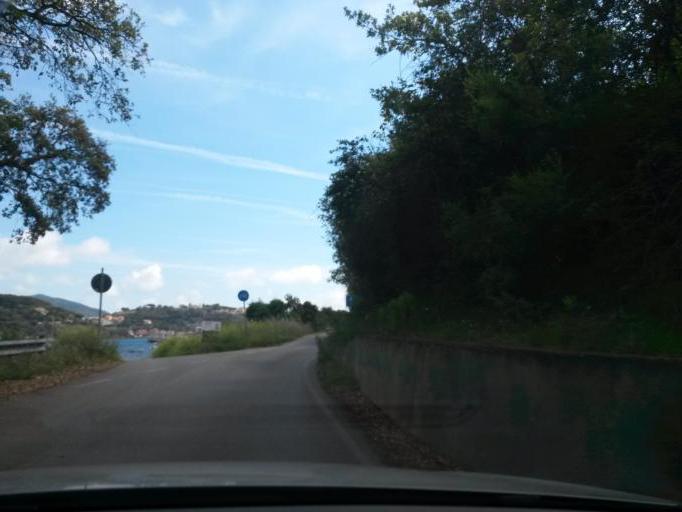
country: IT
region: Tuscany
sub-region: Provincia di Livorno
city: Porto Azzurro
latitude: 42.7576
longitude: 10.3869
